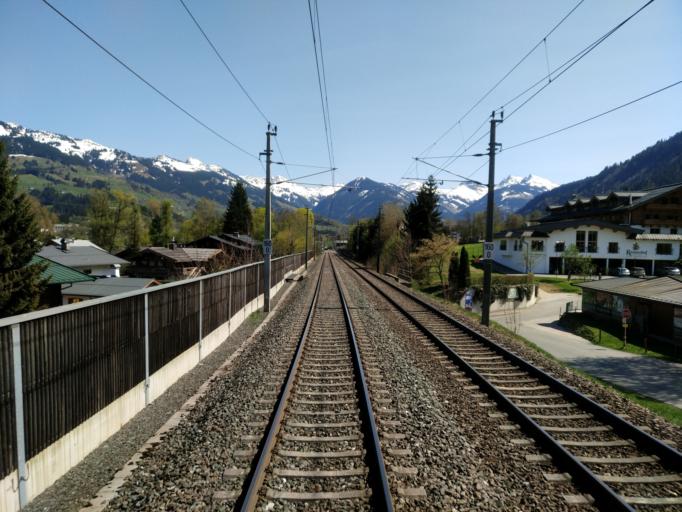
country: AT
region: Tyrol
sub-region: Politischer Bezirk Kitzbuhel
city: Kitzbuhel
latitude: 47.4460
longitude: 12.3846
